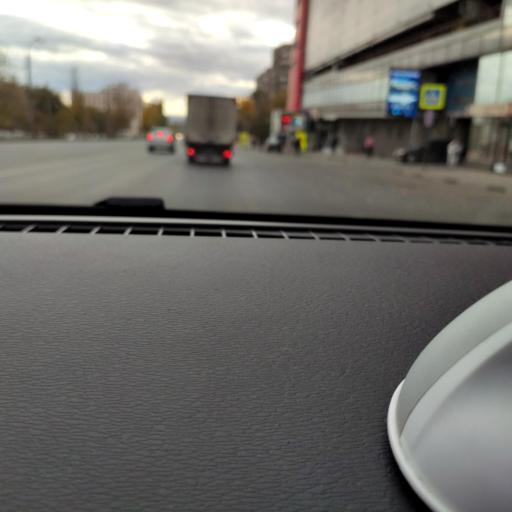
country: RU
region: Samara
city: Samara
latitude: 53.1900
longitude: 50.1910
